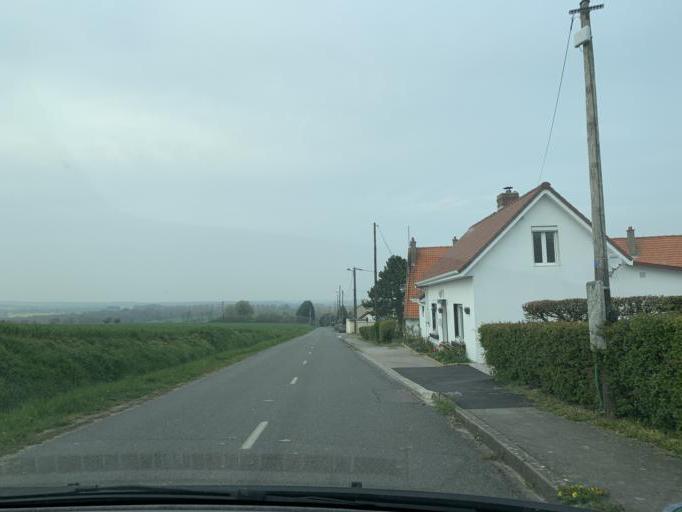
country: FR
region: Nord-Pas-de-Calais
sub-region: Departement du Pas-de-Calais
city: Samer
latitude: 50.6462
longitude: 1.7517
